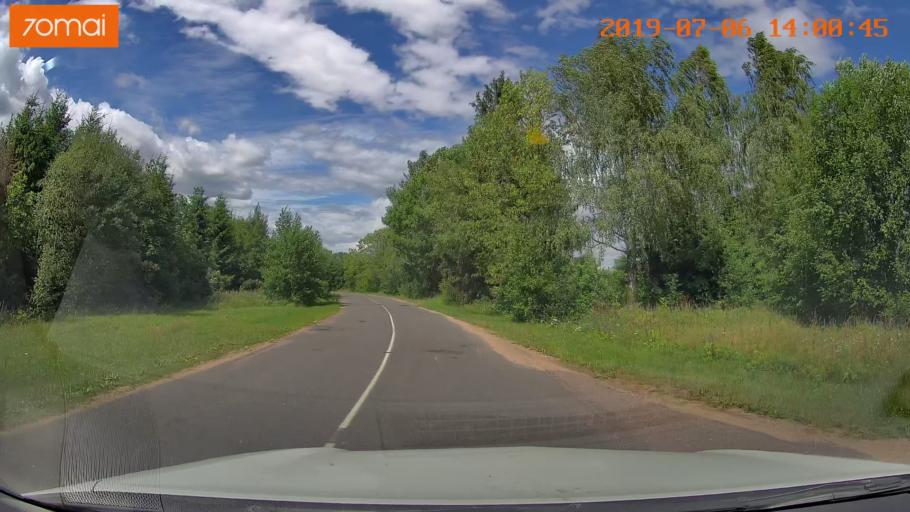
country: BY
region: Minsk
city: Ivyanyets
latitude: 53.8018
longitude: 26.8193
